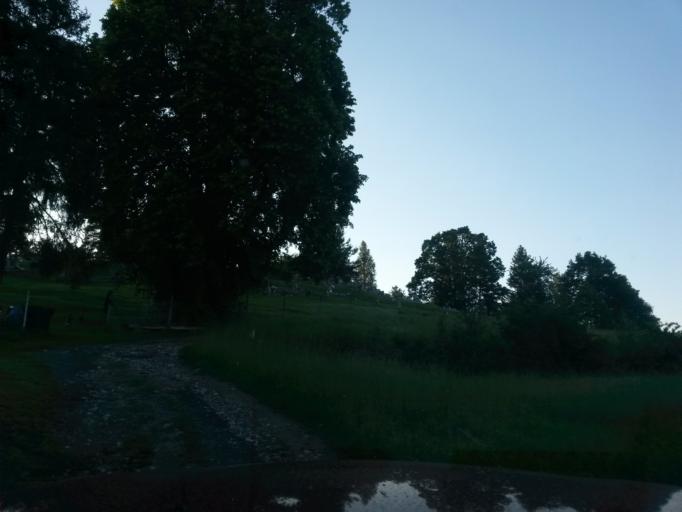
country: UA
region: Zakarpattia
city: Velykyi Bereznyi
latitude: 48.8251
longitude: 22.3582
